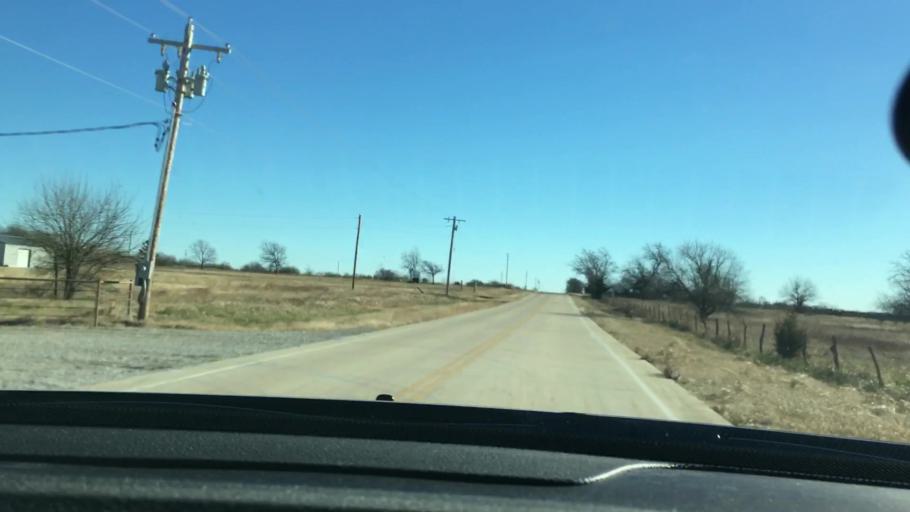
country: US
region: Oklahoma
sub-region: Marshall County
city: Madill
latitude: 34.1144
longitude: -96.6601
